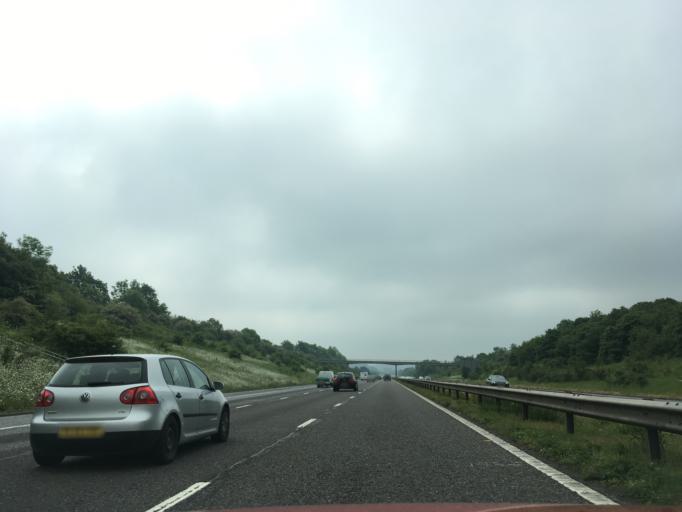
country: GB
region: England
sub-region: North Somerset
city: St. Georges
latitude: 51.3423
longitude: -2.8947
